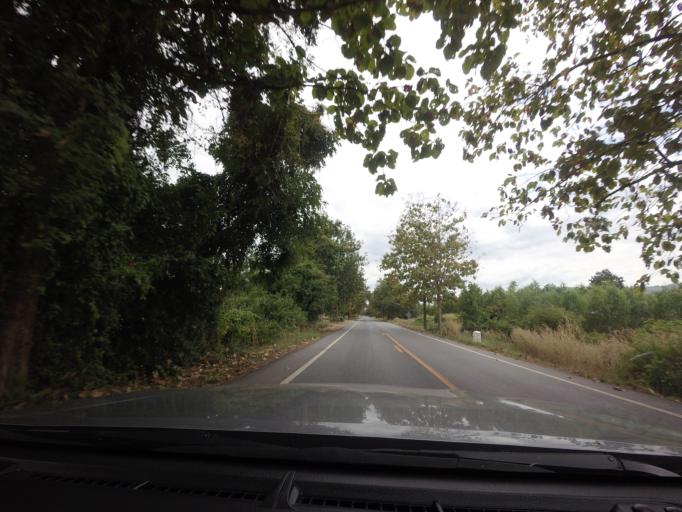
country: TH
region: Phitsanulok
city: Noen Maprang
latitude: 16.6890
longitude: 100.5335
